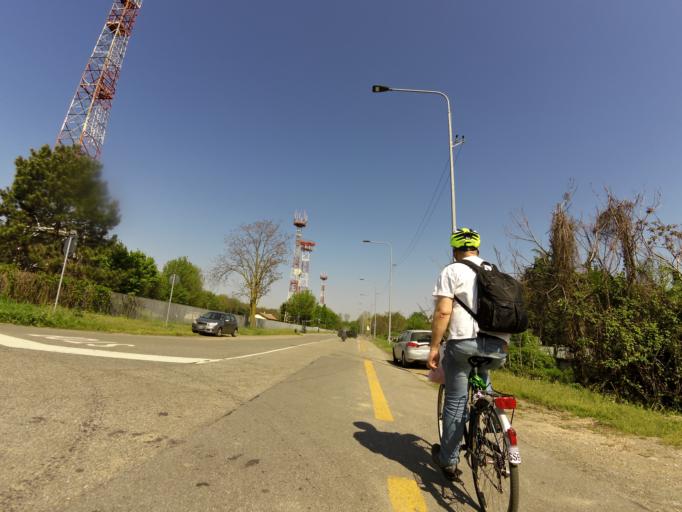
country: IT
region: Lombardy
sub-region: Citta metropolitana di Milano
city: Linate
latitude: 45.4553
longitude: 9.2597
